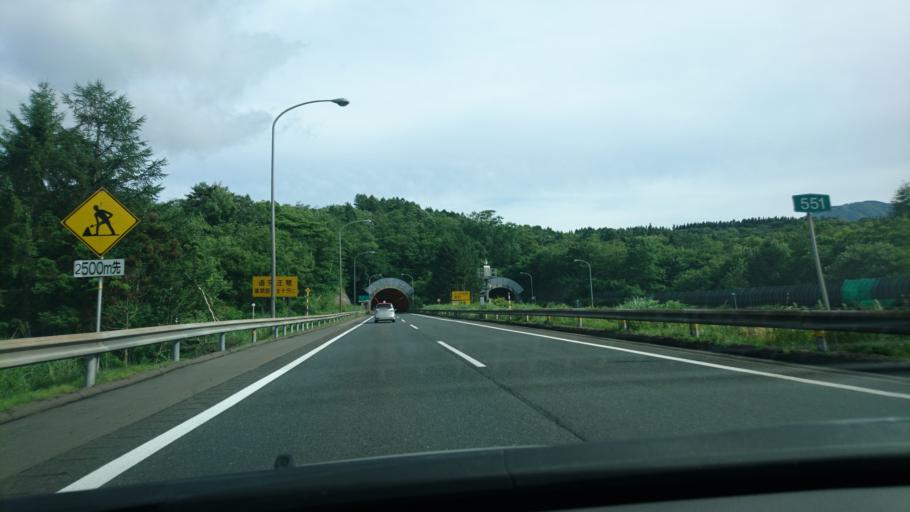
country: JP
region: Akita
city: Hanawa
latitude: 40.0214
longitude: 140.9842
